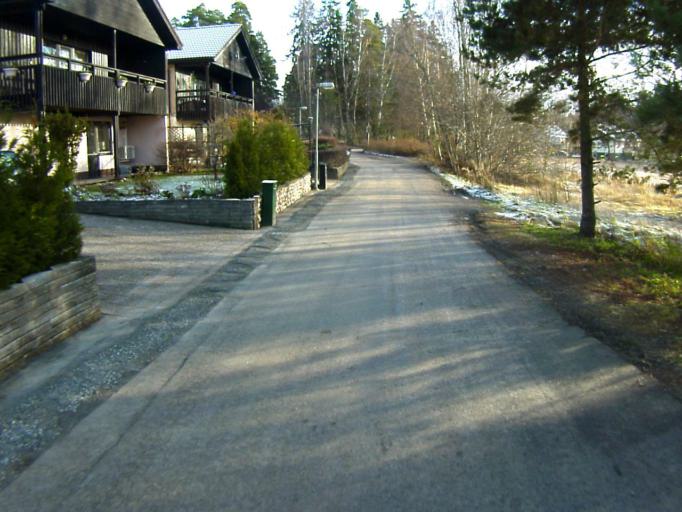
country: SE
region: Soedermanland
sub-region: Eskilstuna Kommun
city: Hallbybrunn
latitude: 59.3896
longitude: 16.4281
